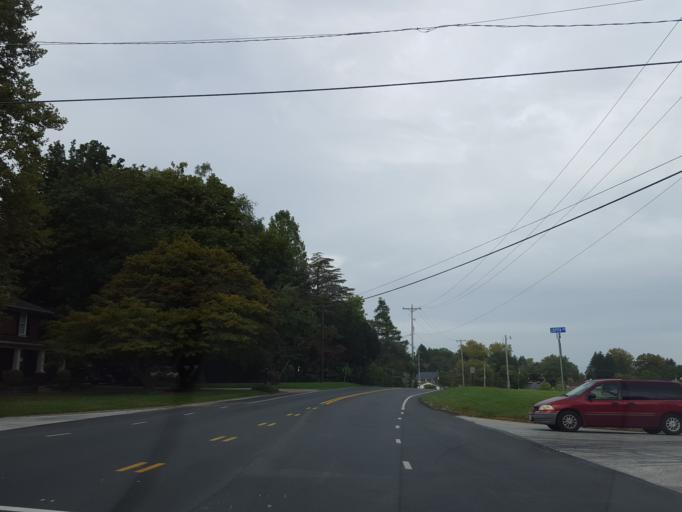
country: US
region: Pennsylvania
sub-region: York County
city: Spry
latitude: 39.9097
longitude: -76.7079
